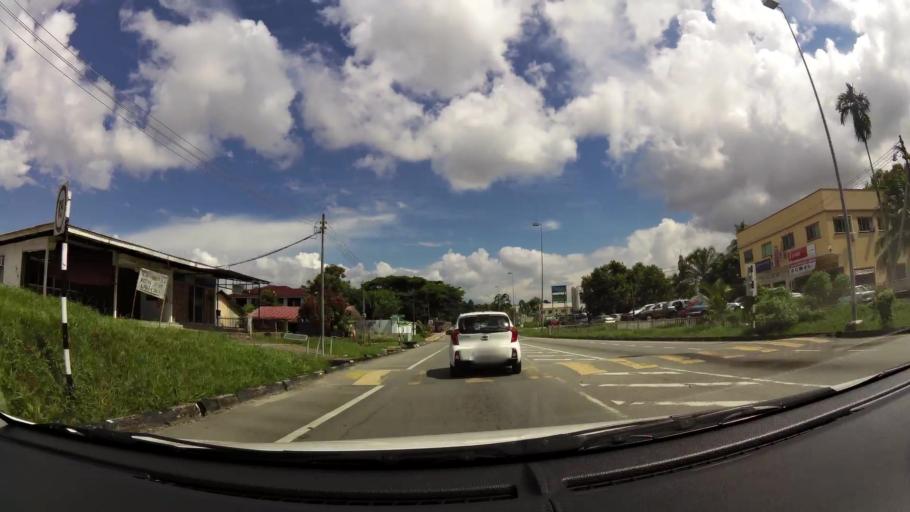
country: BN
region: Brunei and Muara
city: Bandar Seri Begawan
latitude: 4.9706
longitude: 114.9456
